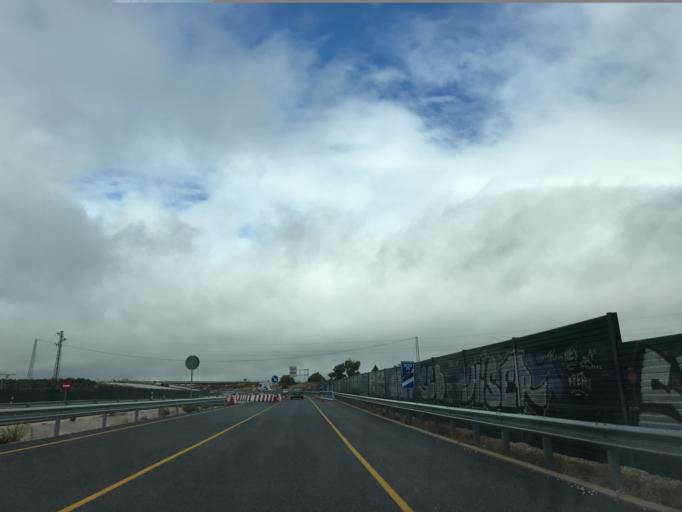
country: ES
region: Andalusia
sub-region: Provincia de Jaen
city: Ubeda
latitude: 38.0210
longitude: -3.4135
